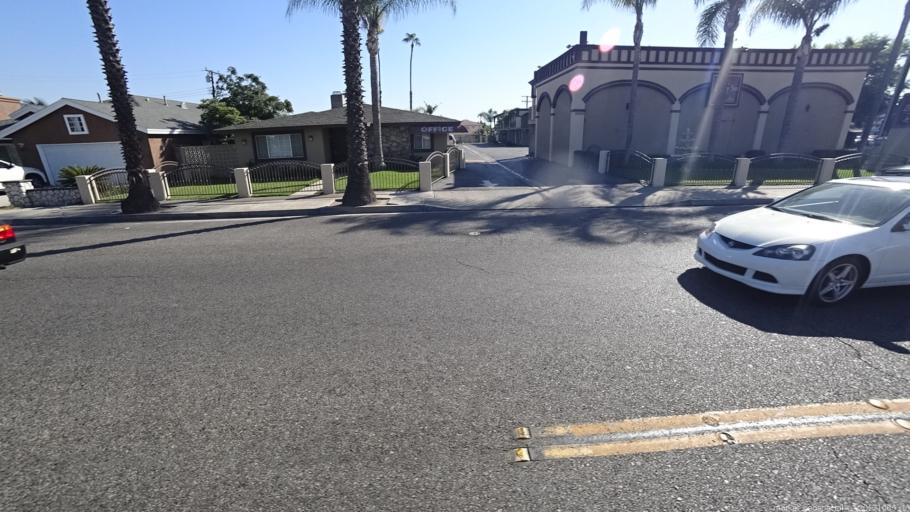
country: US
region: California
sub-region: Orange County
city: Garden Grove
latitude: 33.7817
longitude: -117.9137
